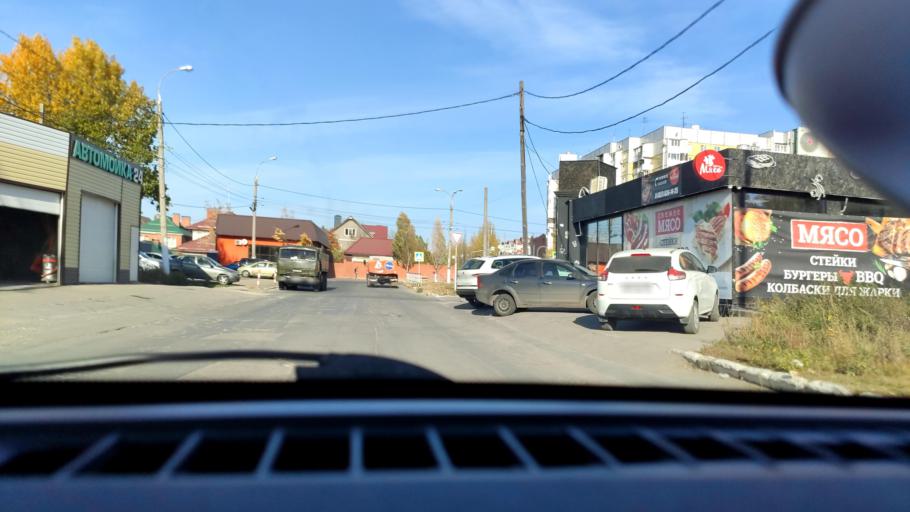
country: RU
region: Samara
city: Samara
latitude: 53.2653
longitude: 50.2118
